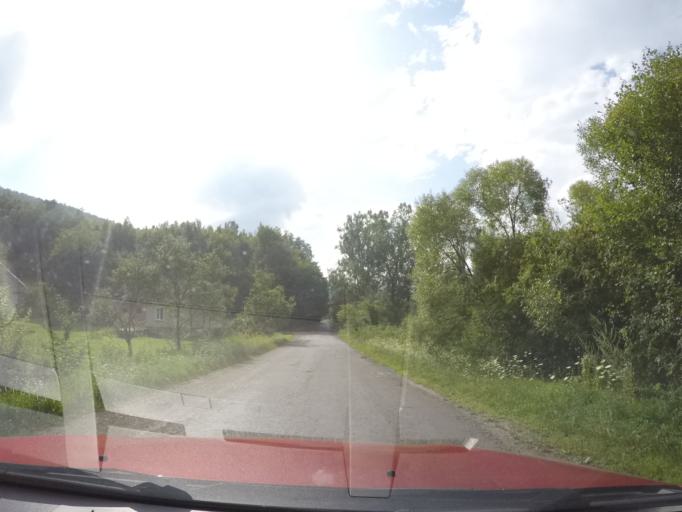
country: UA
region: Zakarpattia
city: Velykyi Bereznyi
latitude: 48.9506
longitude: 22.6114
